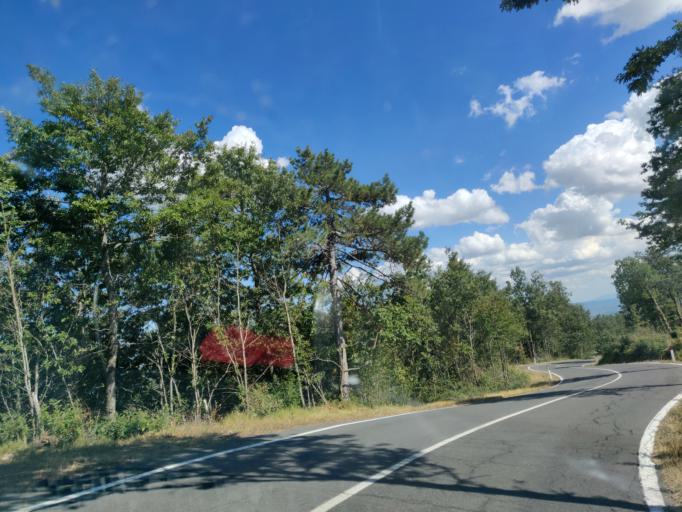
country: IT
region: Tuscany
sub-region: Provincia di Siena
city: Abbadia San Salvatore
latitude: 42.9101
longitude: 11.6921
